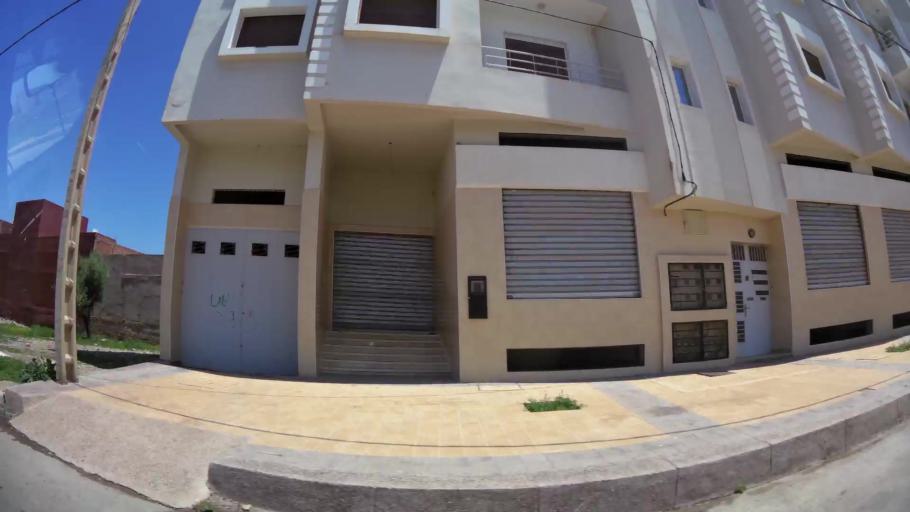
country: MA
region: Oriental
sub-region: Oujda-Angad
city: Oujda
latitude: 34.6853
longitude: -1.8936
